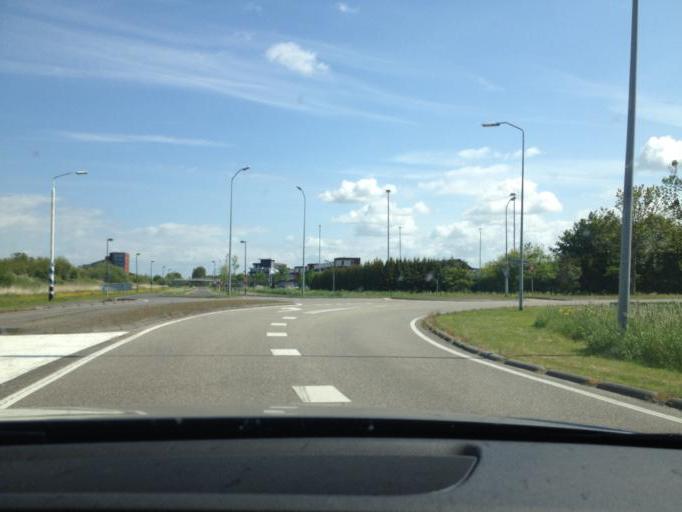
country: NL
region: Flevoland
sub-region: Gemeente Lelystad
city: Lelystad
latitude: 52.5077
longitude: 5.4301
